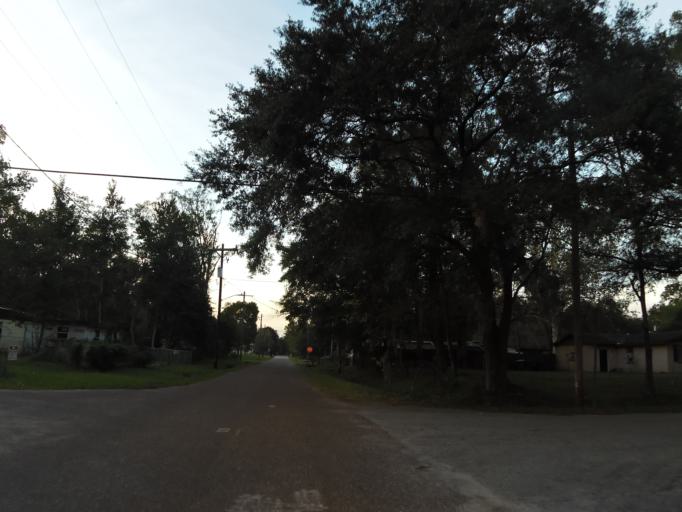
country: US
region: Florida
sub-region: Duval County
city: Jacksonville
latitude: 30.3564
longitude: -81.7352
